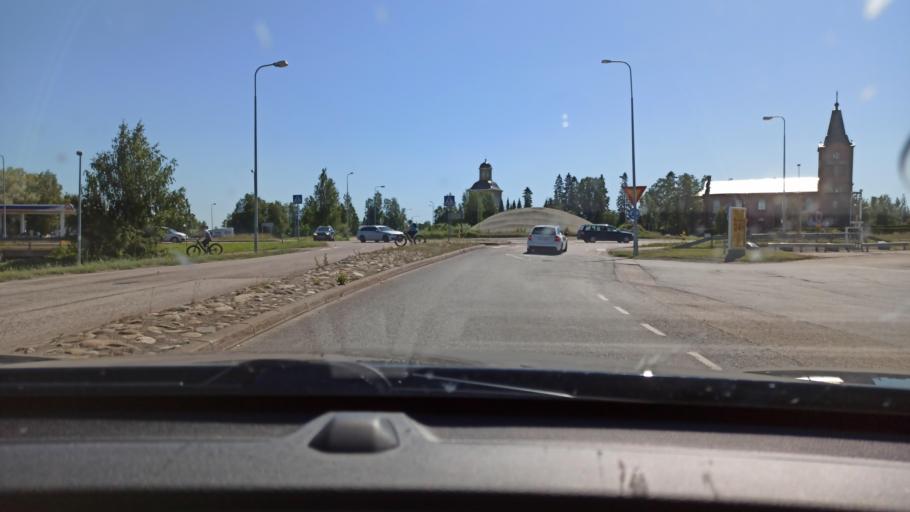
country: FI
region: Northern Ostrobothnia
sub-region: Ylivieska
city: Kalajoki
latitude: 64.2564
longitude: 23.9366
